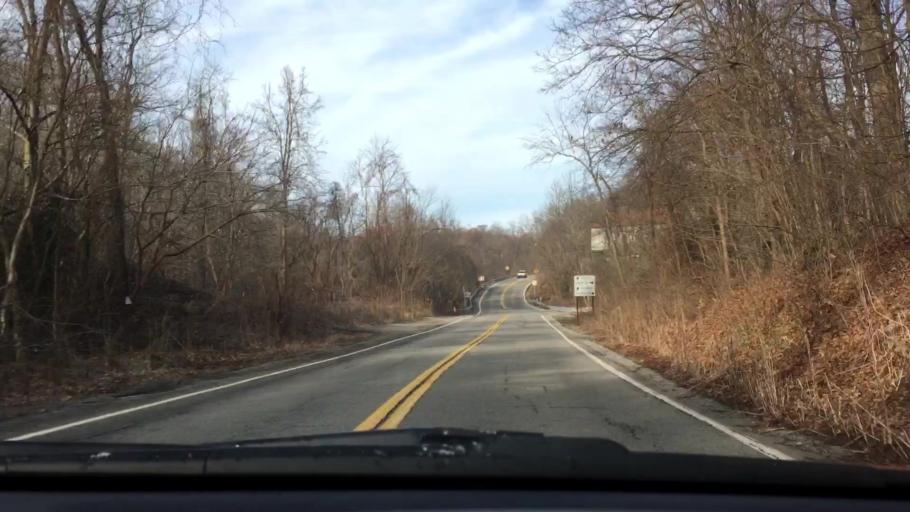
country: US
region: Pennsylvania
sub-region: Allegheny County
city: Industry
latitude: 40.2409
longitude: -79.8386
